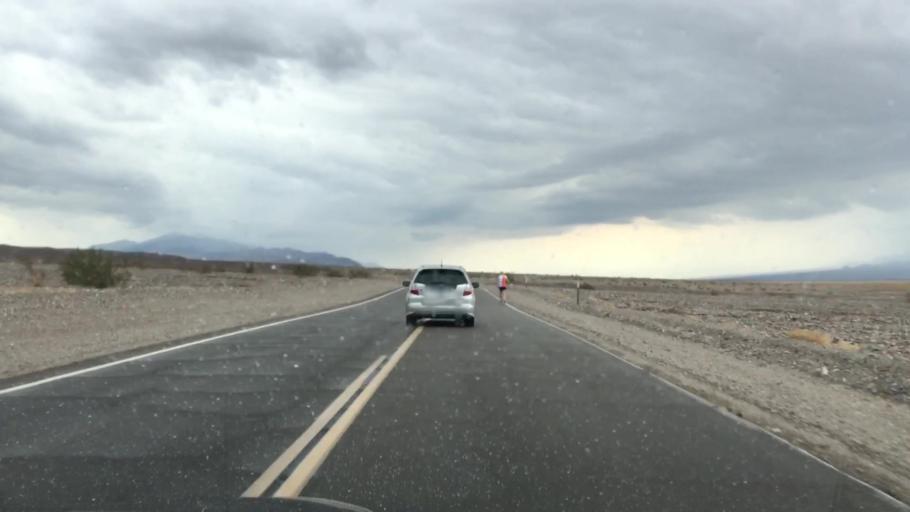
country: US
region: Nevada
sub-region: Nye County
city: Beatty
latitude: 36.5365
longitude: -116.8840
